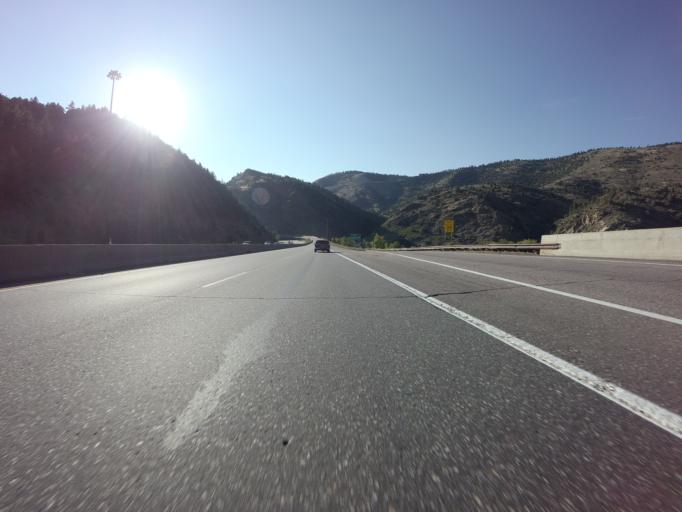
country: US
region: Colorado
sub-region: Clear Creek County
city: Idaho Springs
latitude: 39.7441
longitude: -105.4345
